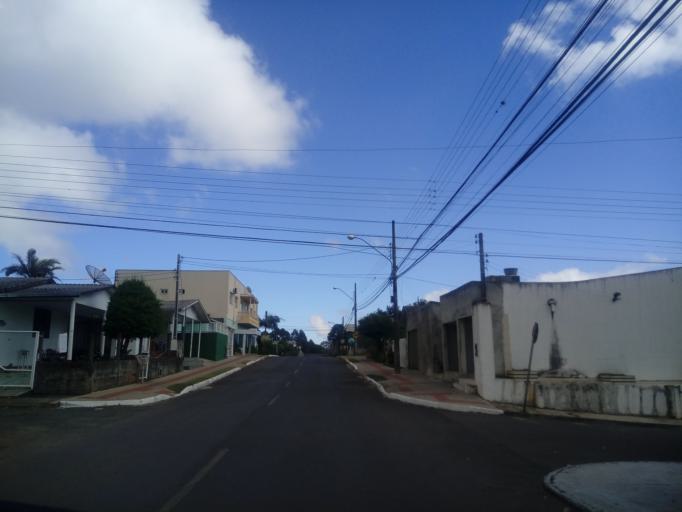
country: BR
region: Santa Catarina
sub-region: Chapeco
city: Chapeco
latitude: -27.1163
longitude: -52.6265
